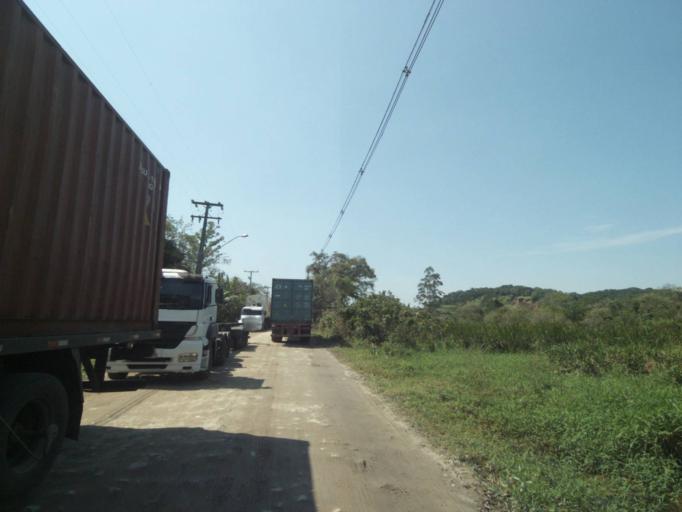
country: BR
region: Parana
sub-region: Paranagua
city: Paranagua
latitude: -25.5587
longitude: -48.6027
